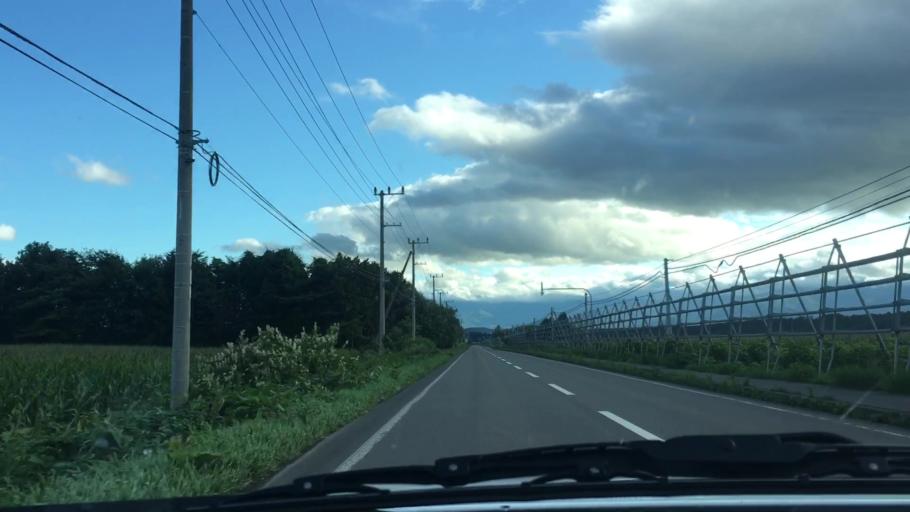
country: JP
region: Hokkaido
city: Otofuke
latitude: 43.1432
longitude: 142.8969
